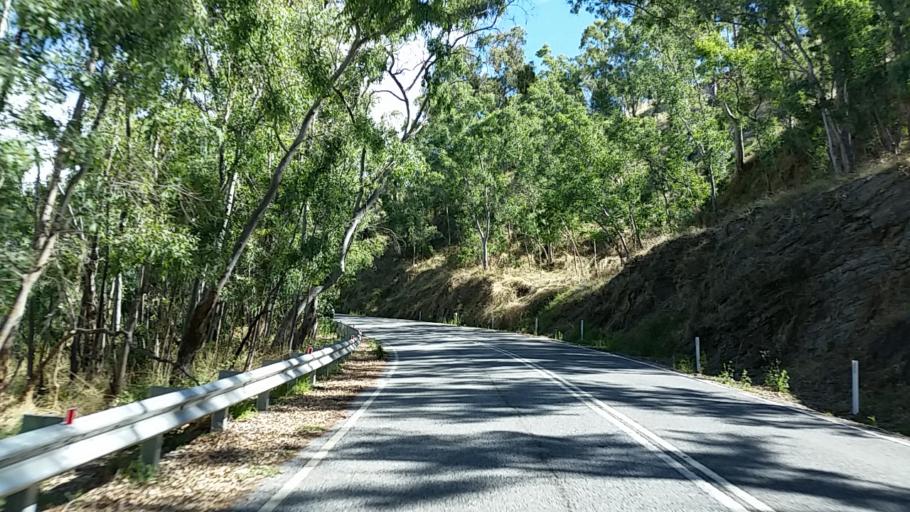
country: AU
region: South Australia
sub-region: Tea Tree Gully
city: Golden Grove
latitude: -34.8535
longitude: 138.7911
